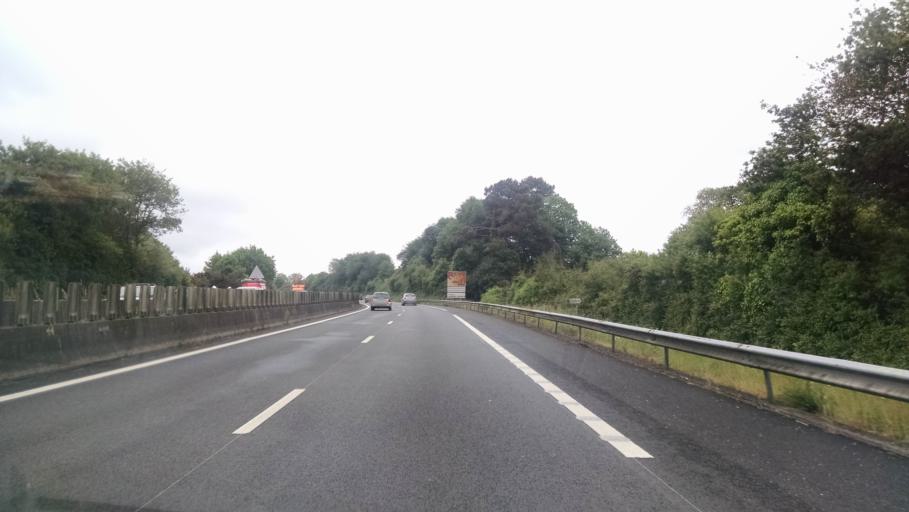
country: FR
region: Brittany
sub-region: Departement du Morbihan
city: Plougoumelen
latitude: 47.6676
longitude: -2.9186
